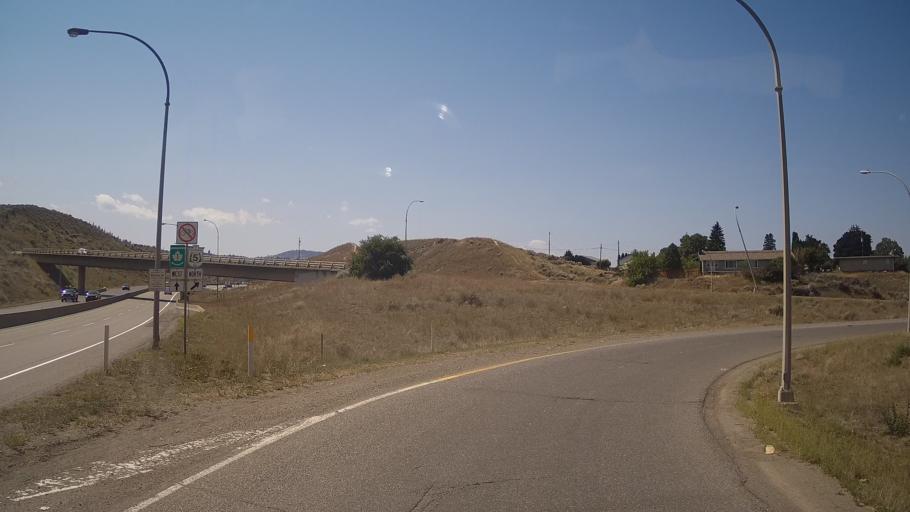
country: CA
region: British Columbia
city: Kamloops
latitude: 50.6718
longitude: -120.3009
